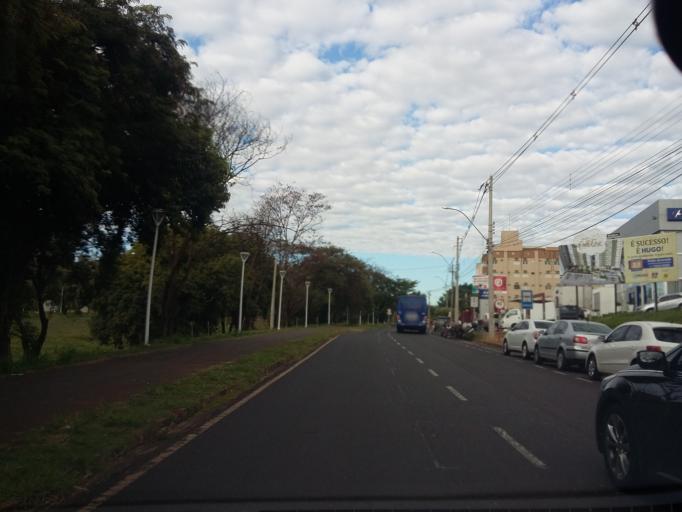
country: BR
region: Sao Paulo
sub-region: Sao Jose Do Rio Preto
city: Sao Jose do Rio Preto
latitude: -20.8313
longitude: -49.4055
